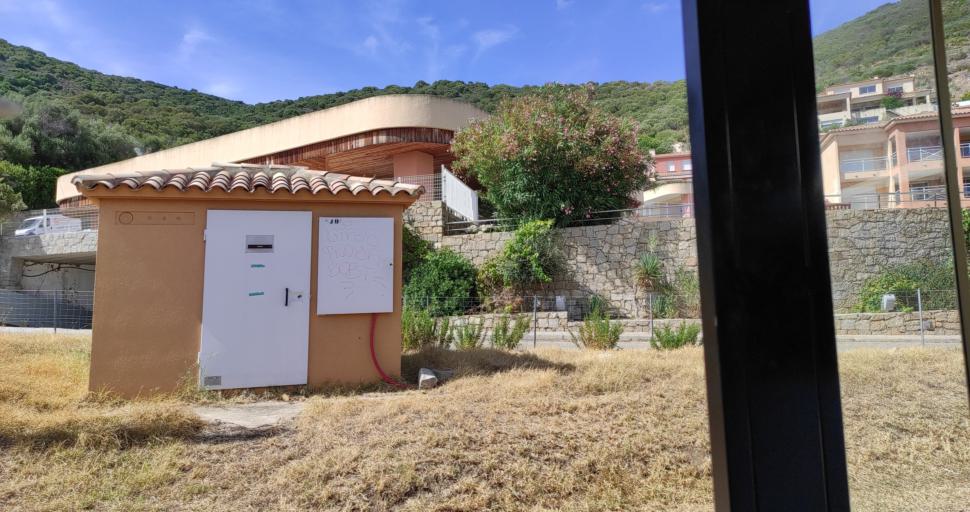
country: FR
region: Corsica
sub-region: Departement de la Corse-du-Sud
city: Ajaccio
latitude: 41.9077
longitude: 8.6321
